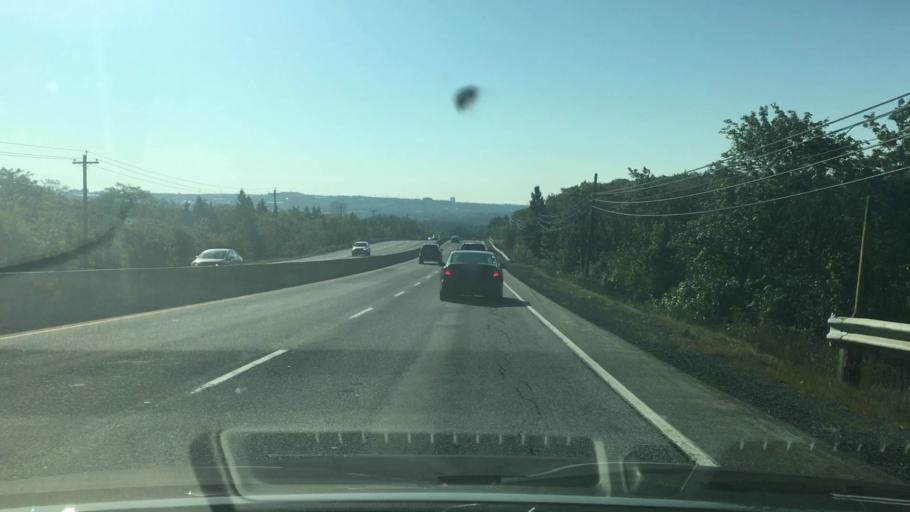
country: CA
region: Nova Scotia
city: Dartmouth
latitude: 44.7148
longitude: -63.6314
